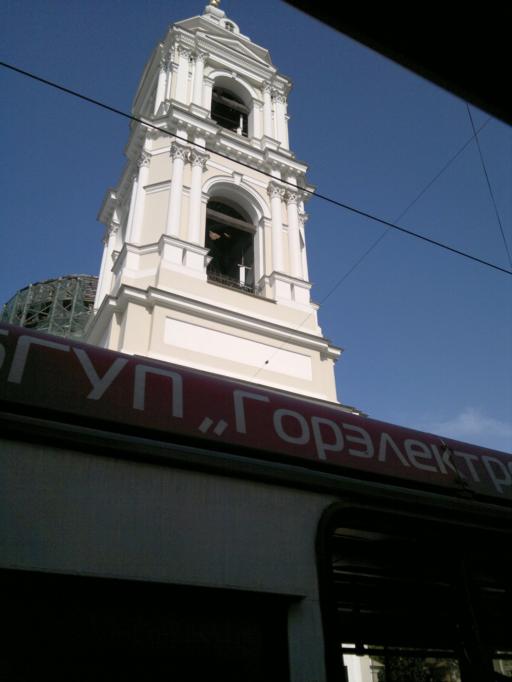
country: RU
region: St.-Petersburg
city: Saint Petersburg
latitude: 59.9462
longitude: 30.2851
